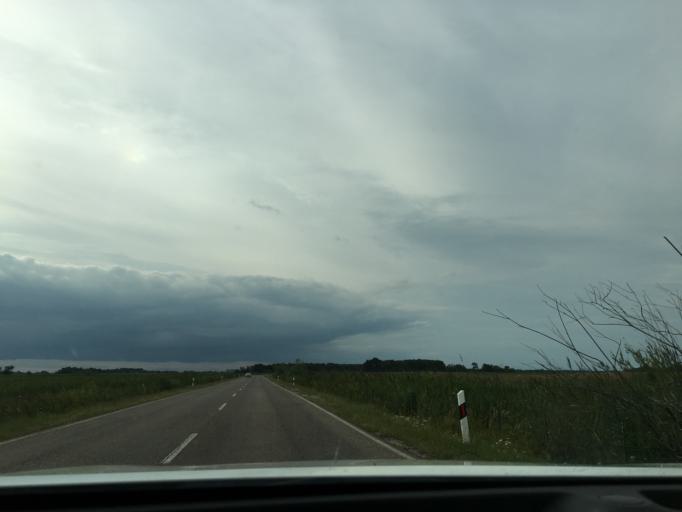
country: HU
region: Hajdu-Bihar
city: Egyek
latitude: 47.5571
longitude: 20.8690
